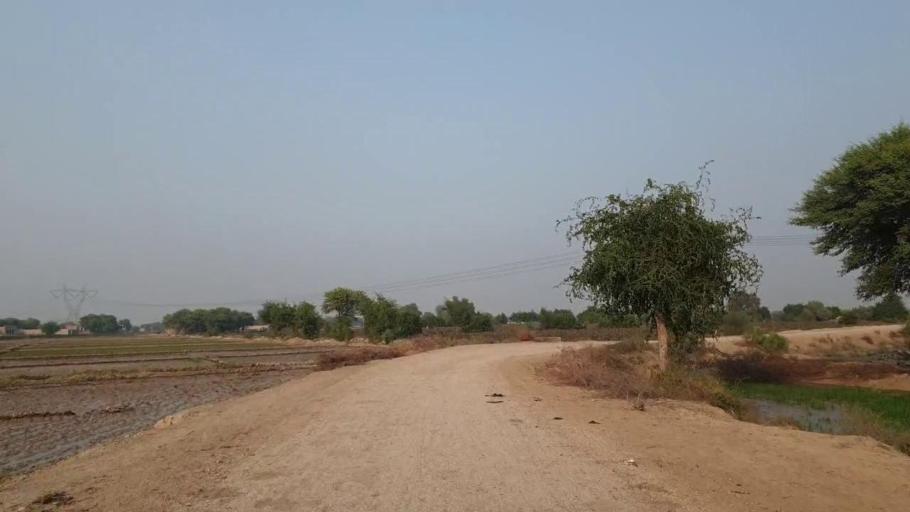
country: PK
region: Sindh
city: Bhan
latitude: 26.4998
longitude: 67.7513
